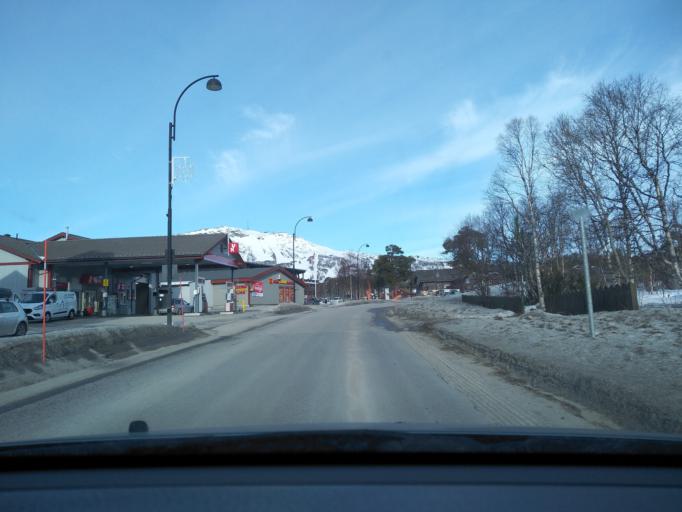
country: NO
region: Aust-Agder
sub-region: Bykle
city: Hovden
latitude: 59.5590
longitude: 7.3570
